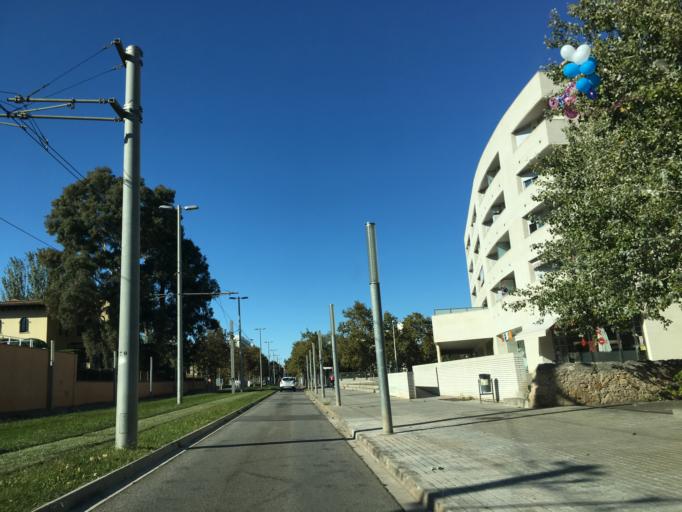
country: ES
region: Catalonia
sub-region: Provincia de Barcelona
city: Sant Joan Despi
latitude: 41.3580
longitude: 2.0649
